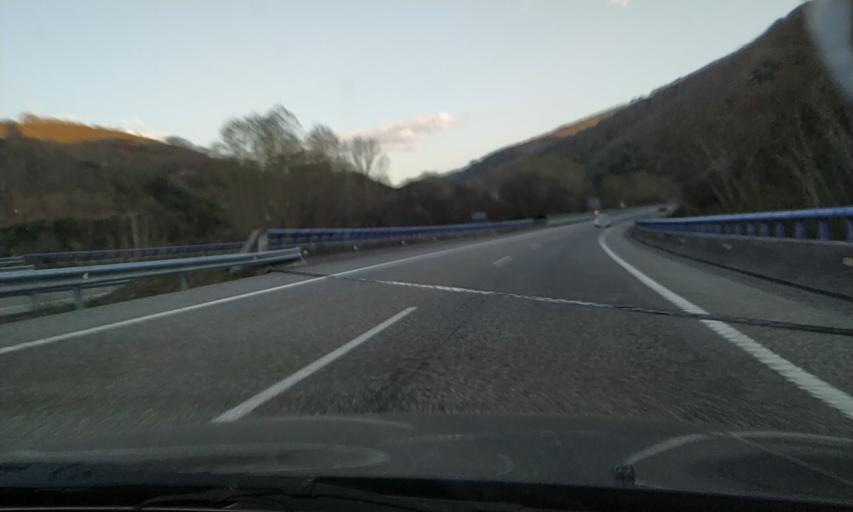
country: ES
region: Castille and Leon
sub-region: Provincia de Leon
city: Trabadelo
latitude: 42.6536
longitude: -6.8919
